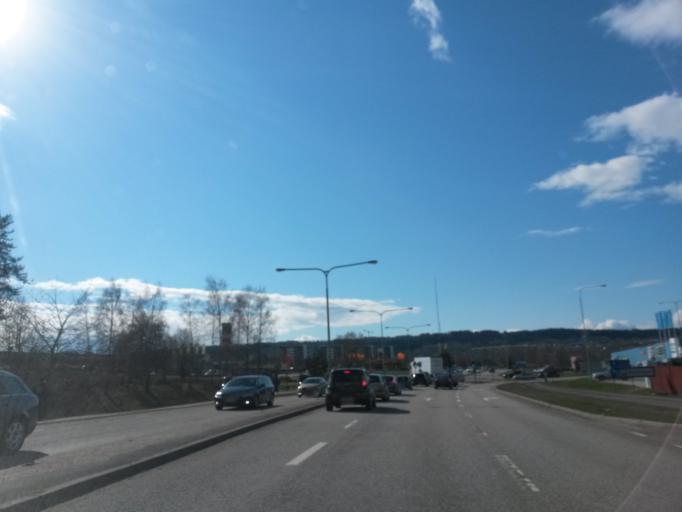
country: SE
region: Vaestra Goetaland
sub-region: Skovde Kommun
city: Skoevde
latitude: 58.4067
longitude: 13.8598
